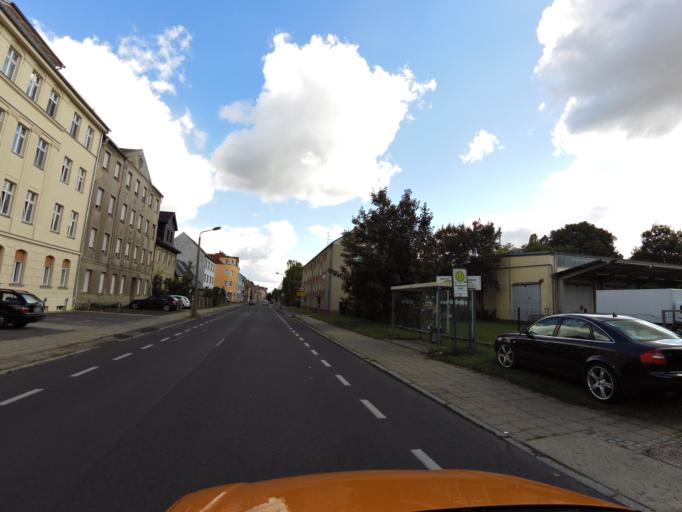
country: DE
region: Brandenburg
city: Luckenwalde
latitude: 52.0951
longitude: 13.1578
